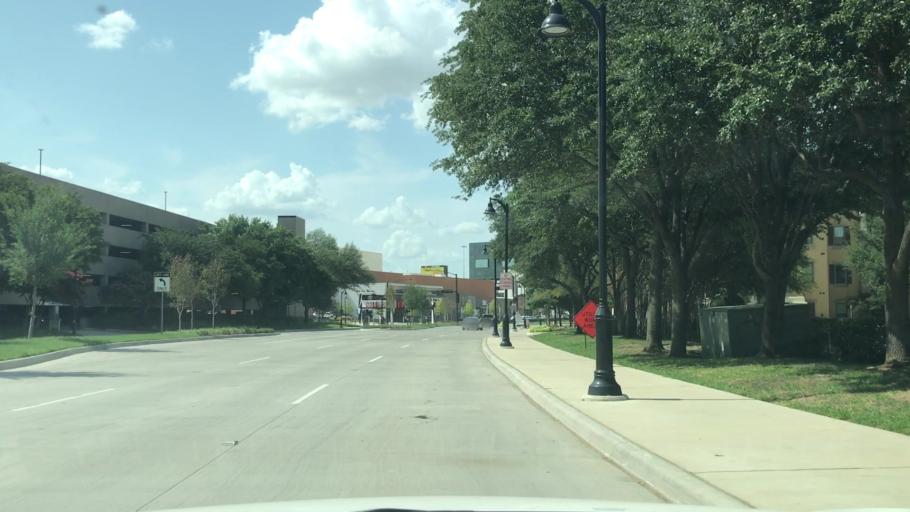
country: US
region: Texas
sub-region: Dallas County
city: Irving
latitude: 32.8716
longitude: -96.9427
